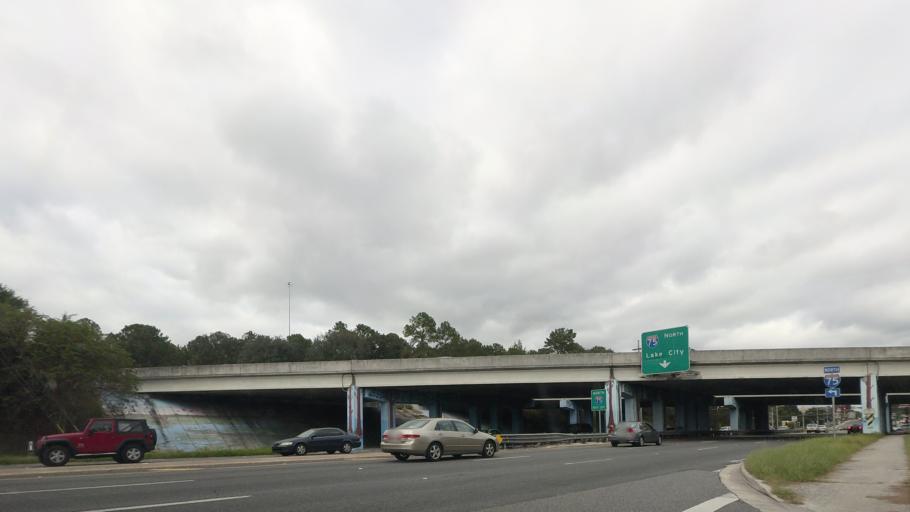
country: US
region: Florida
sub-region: Alachua County
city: Alachua
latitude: 29.6595
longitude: -82.4196
